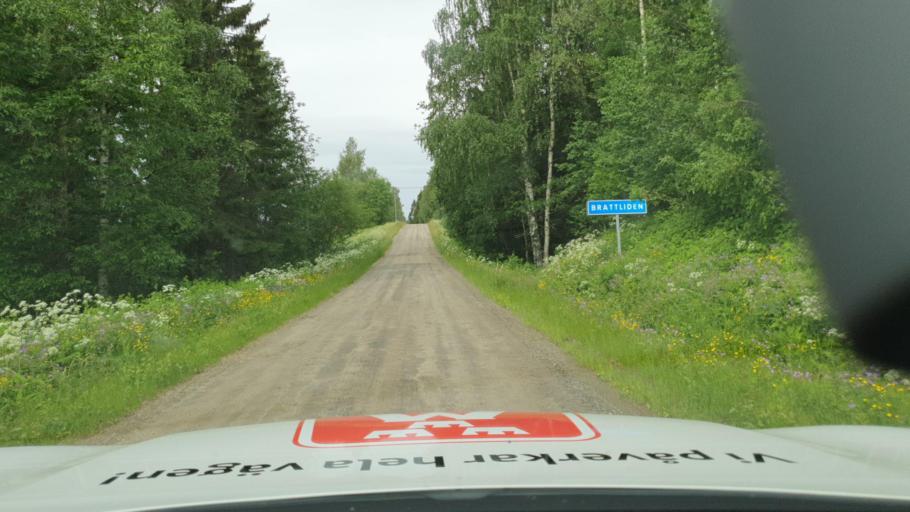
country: SE
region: Vaesterbotten
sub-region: Robertsfors Kommun
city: Robertsfors
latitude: 64.2837
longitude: 20.6724
